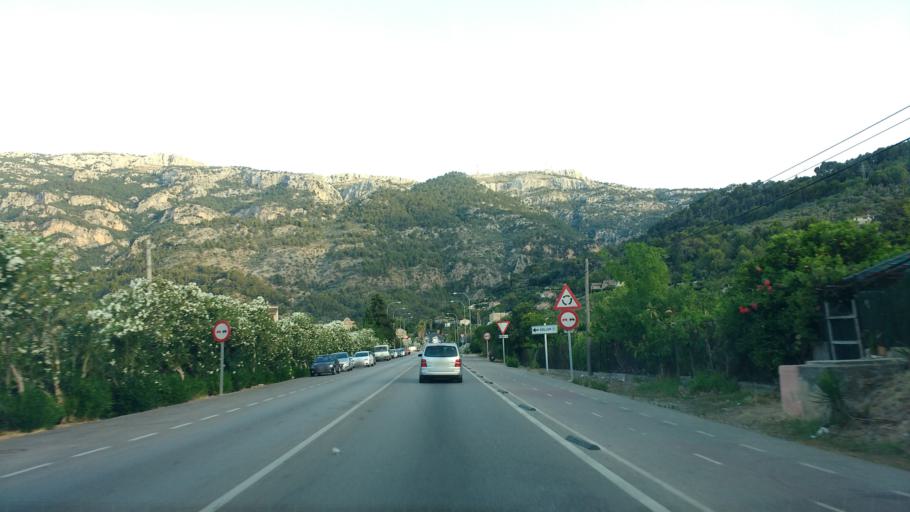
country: ES
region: Balearic Islands
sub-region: Illes Balears
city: Soller
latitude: 39.7685
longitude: 2.7072
